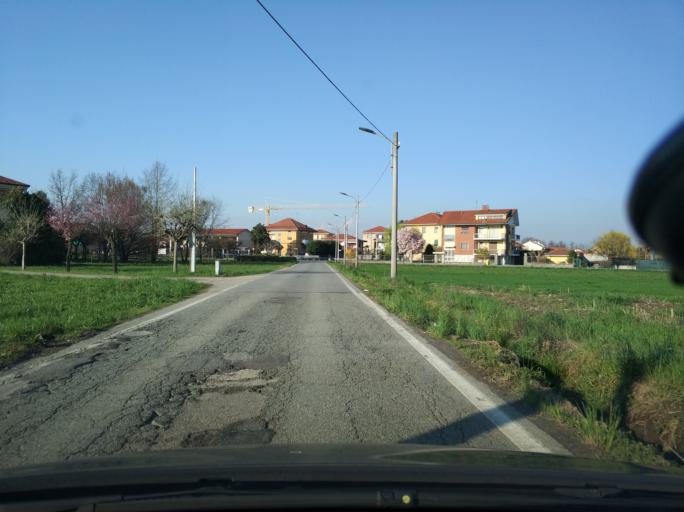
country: IT
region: Piedmont
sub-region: Provincia di Torino
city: San Maurizio
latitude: 45.1979
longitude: 7.6183
